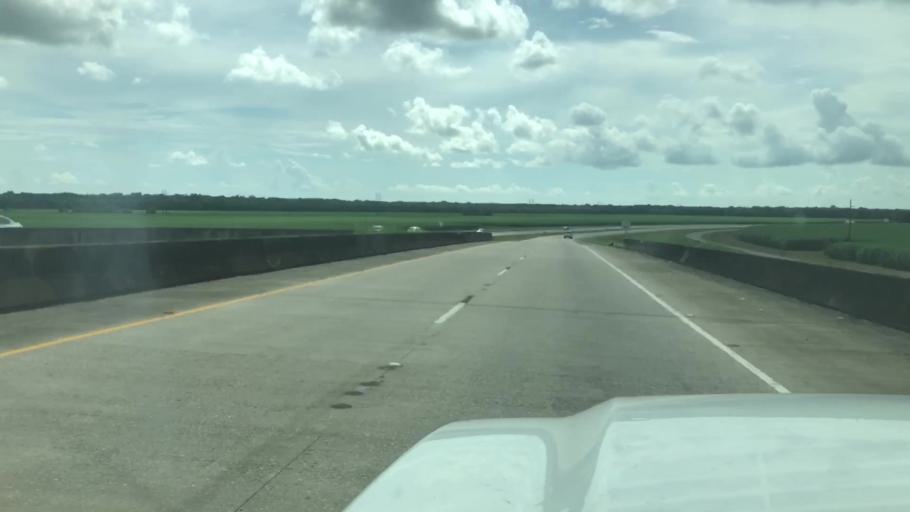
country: US
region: Louisiana
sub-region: Saint Mary Parish
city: Franklin
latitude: 29.7579
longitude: -91.4671
